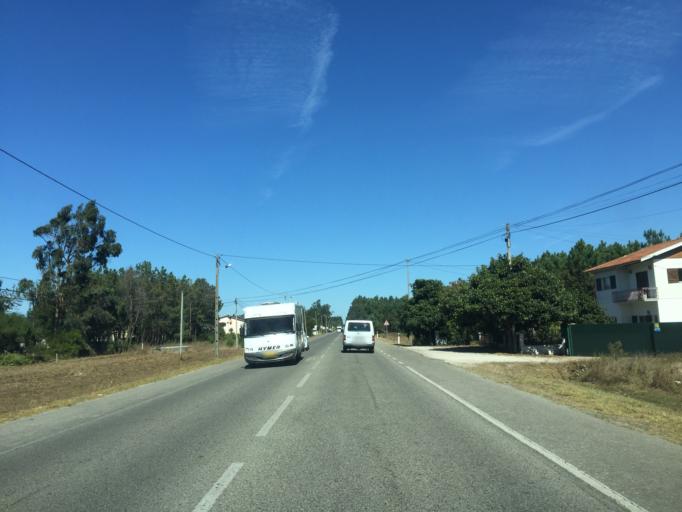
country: PT
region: Coimbra
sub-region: Figueira da Foz
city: Alhadas
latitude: 40.2841
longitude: -8.7695
